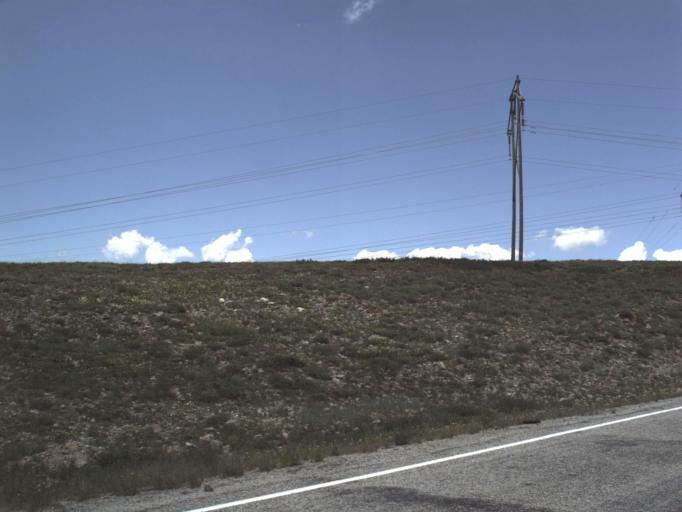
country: US
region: Utah
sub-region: Weber County
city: Wolf Creek
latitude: 41.4080
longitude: -111.5238
